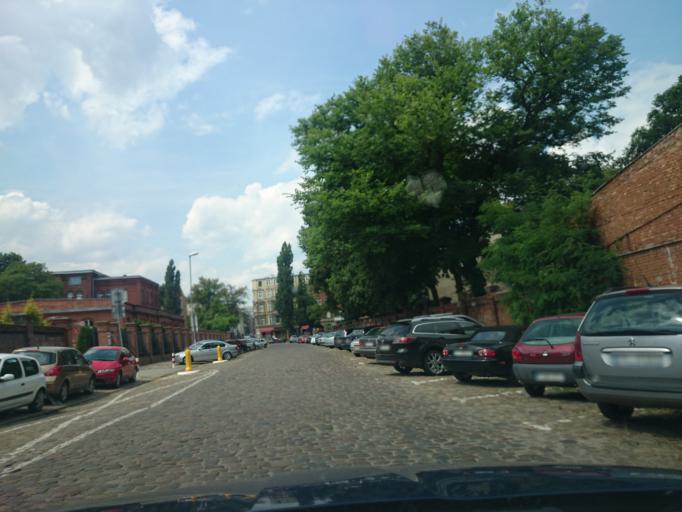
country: PL
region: West Pomeranian Voivodeship
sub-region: Szczecin
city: Szczecin
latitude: 53.4237
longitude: 14.5458
